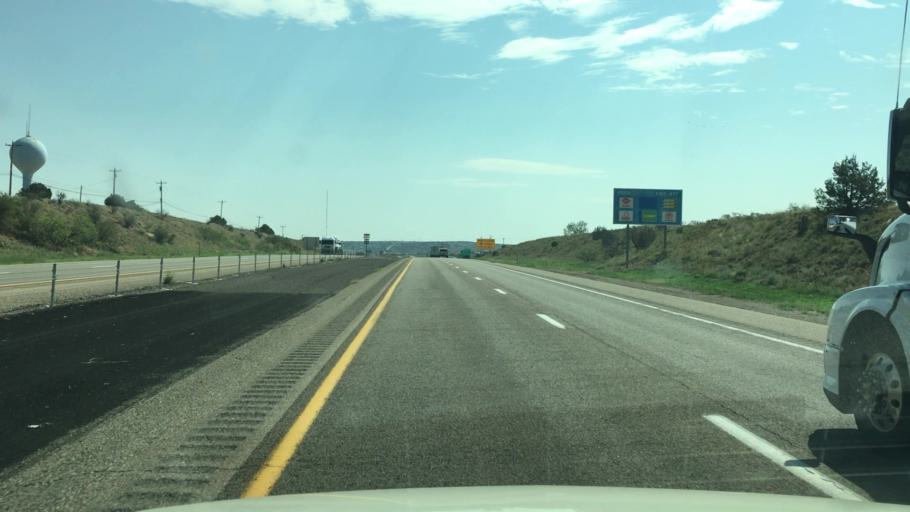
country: US
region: New Mexico
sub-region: Guadalupe County
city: Santa Rosa
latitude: 34.9442
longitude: -104.6610
